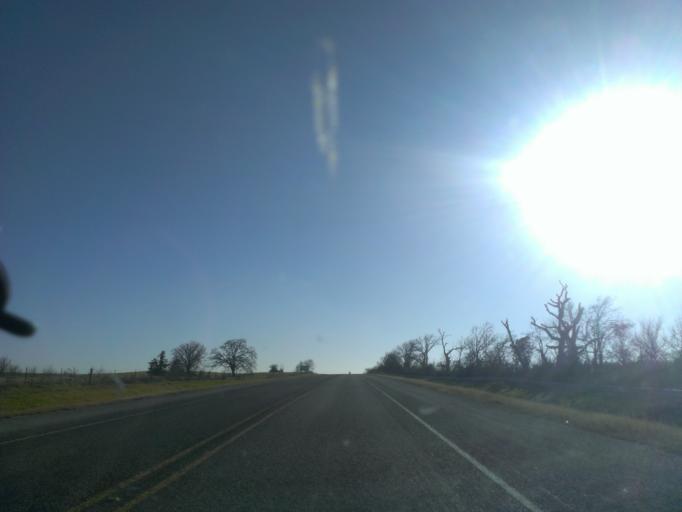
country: US
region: Texas
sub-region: Bastrop County
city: Elgin
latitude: 30.3652
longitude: -97.2650
